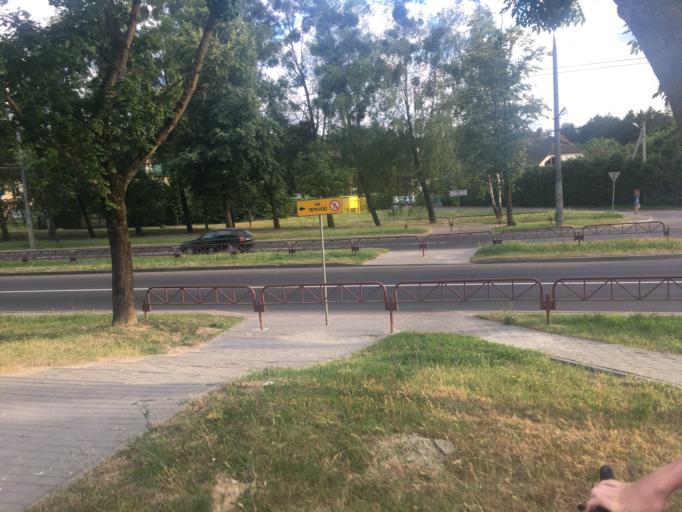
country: BY
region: Grodnenskaya
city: Hrodna
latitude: 53.6846
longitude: 23.8033
